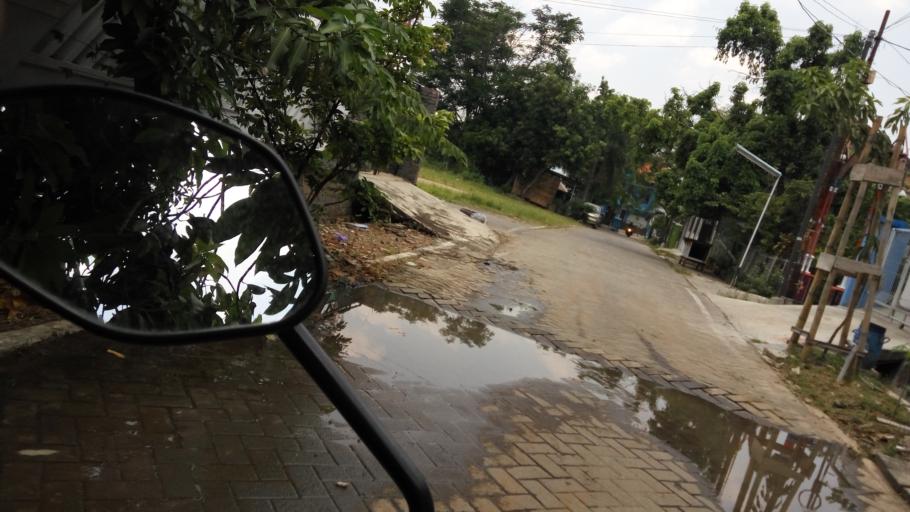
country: ID
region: Central Java
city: Mranggen
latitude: -7.0460
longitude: 110.4758
